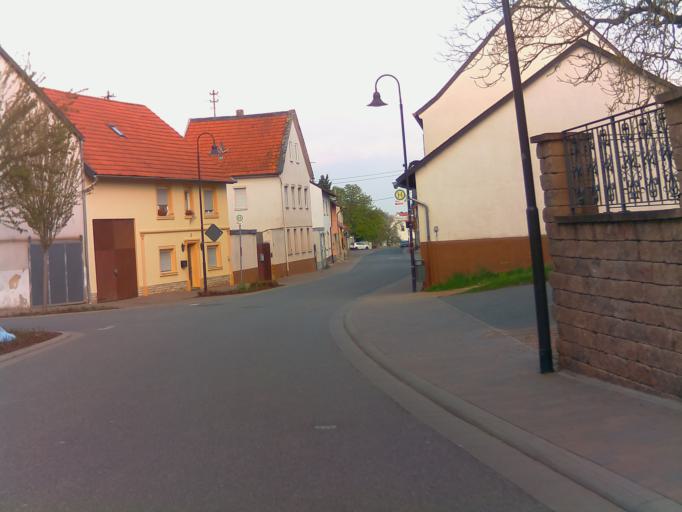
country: DE
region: Rheinland-Pfalz
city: Mandel
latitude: 49.8547
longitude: 7.7711
